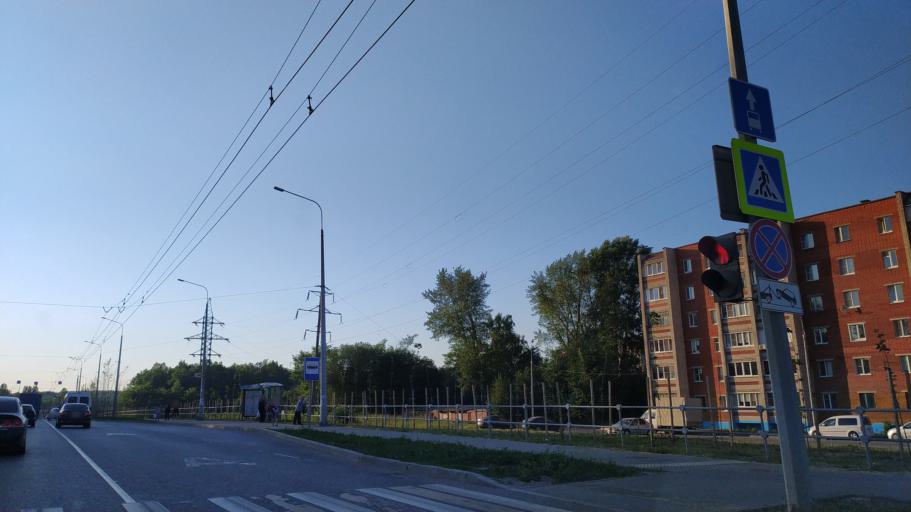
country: RU
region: Chuvashia
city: Kugesi
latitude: 56.0794
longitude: 47.2706
